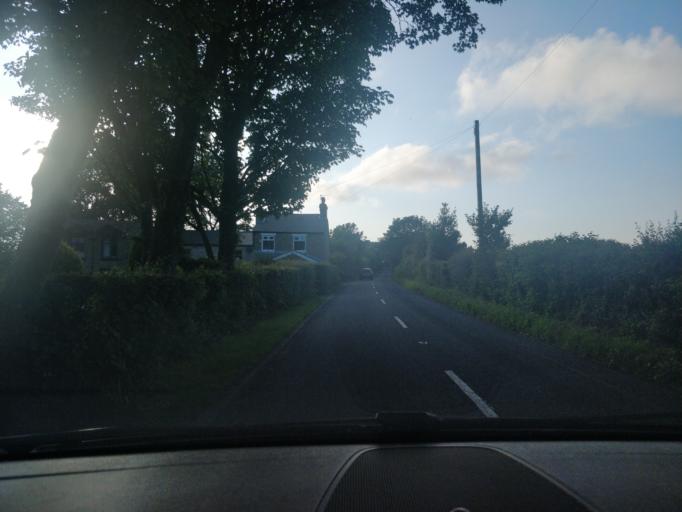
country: GB
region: England
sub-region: Lancashire
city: Skelmersdale
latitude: 53.5590
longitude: -2.7492
